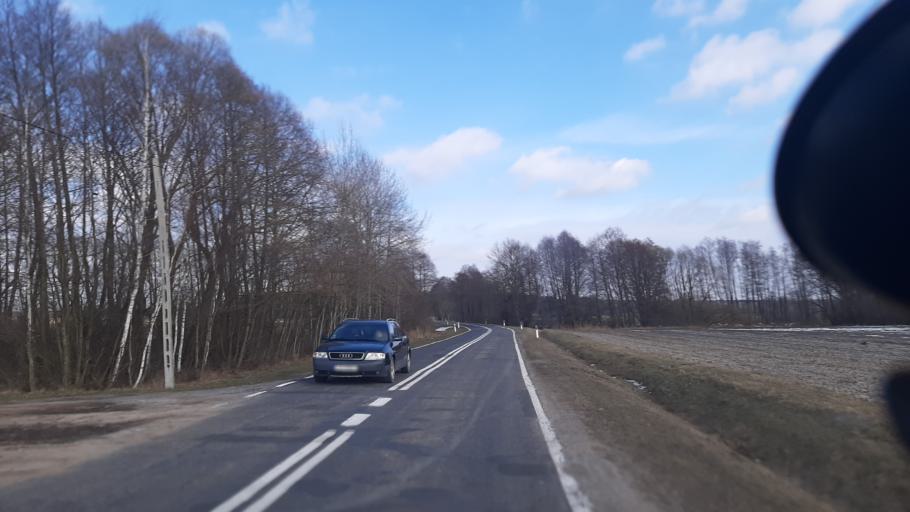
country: PL
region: Lublin Voivodeship
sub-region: Powiat wlodawski
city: Urszulin
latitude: 51.4966
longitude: 23.2421
